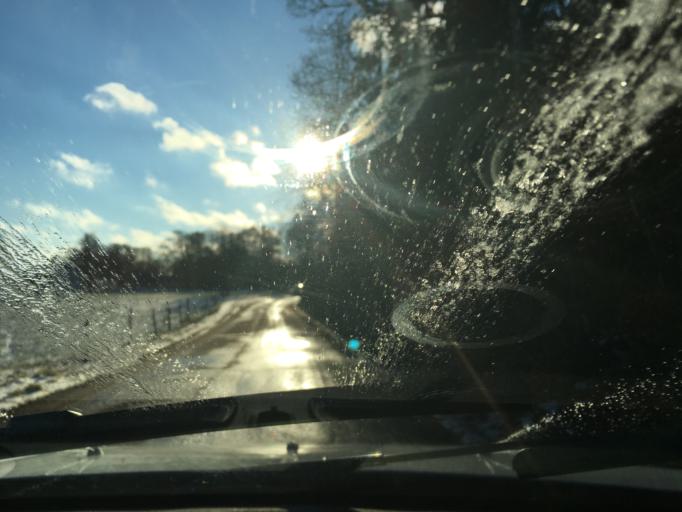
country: SE
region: Vaestra Goetaland
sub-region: Tjorns Kommun
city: Myggenas
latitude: 58.0931
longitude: 11.7555
